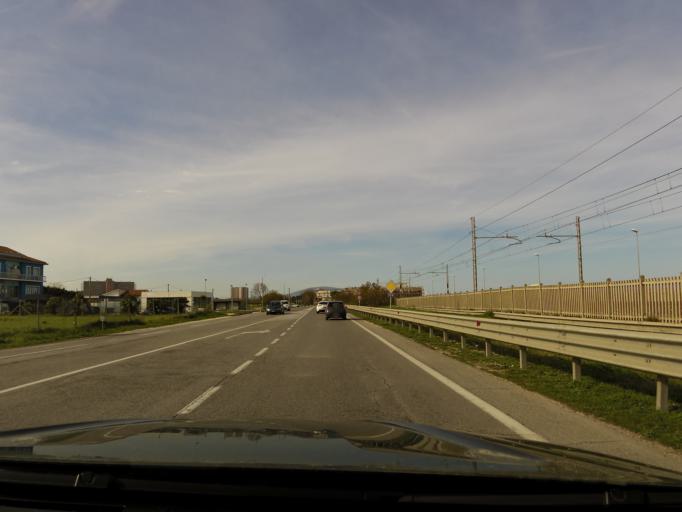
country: IT
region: The Marches
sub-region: Provincia di Macerata
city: Porto Recanati
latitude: 43.4085
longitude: 13.6767
